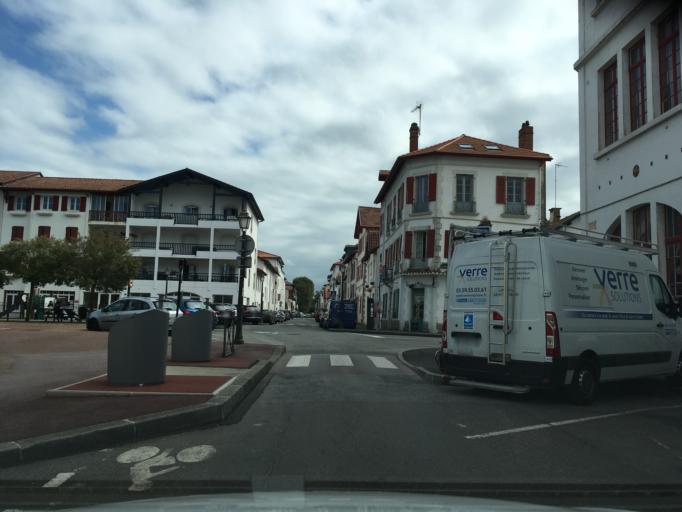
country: FR
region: Aquitaine
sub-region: Departement des Pyrenees-Atlantiques
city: Bayonne
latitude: 43.4942
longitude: -1.4665
